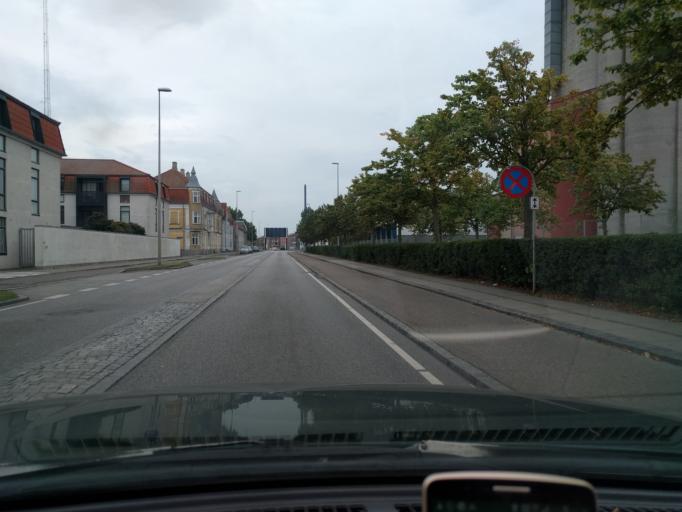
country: DK
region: Zealand
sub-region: Slagelse Kommune
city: Korsor
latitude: 55.3338
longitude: 11.1412
